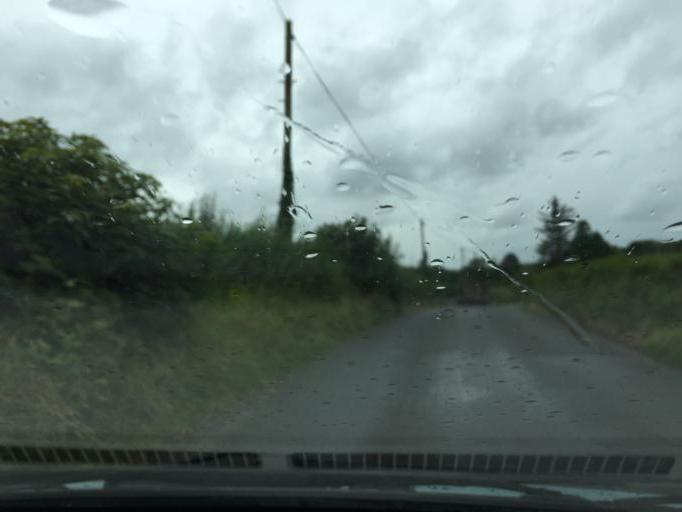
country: IE
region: Connaught
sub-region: Sligo
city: Sligo
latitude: 54.2337
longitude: -8.4530
